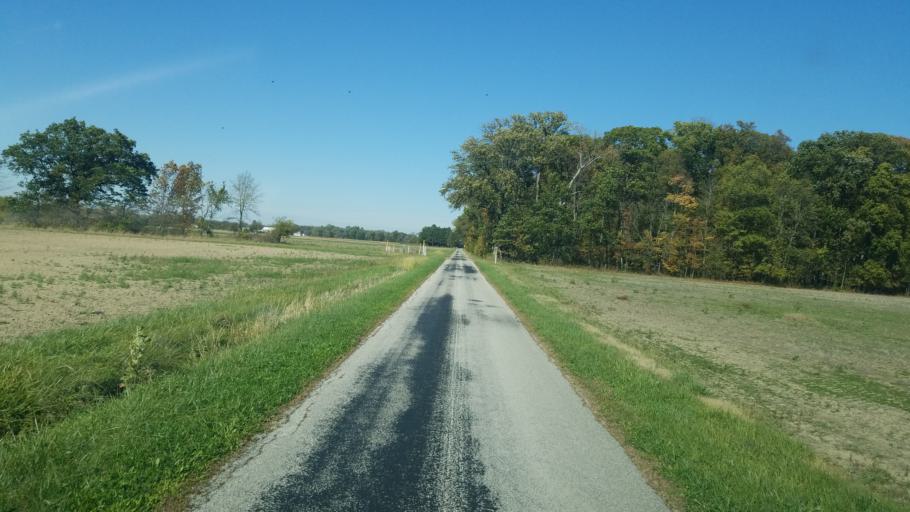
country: US
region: Ohio
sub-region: Marion County
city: Prospect
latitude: 40.5443
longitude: -83.2515
